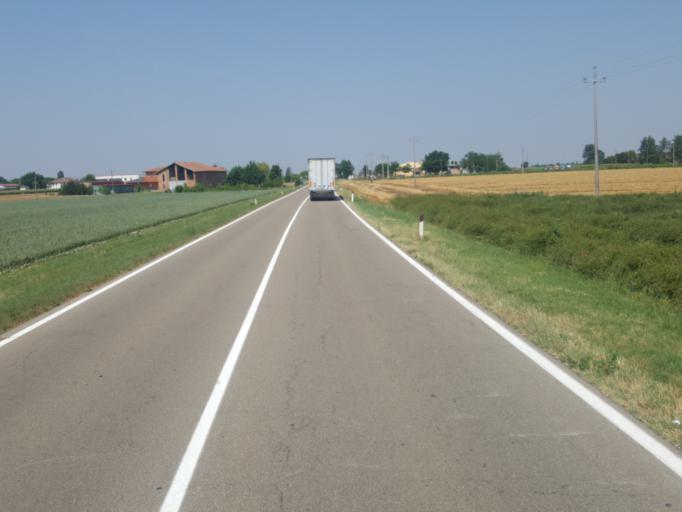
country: IT
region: Emilia-Romagna
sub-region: Provincia di Bologna
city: Sesto Imolese
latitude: 44.4671
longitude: 11.7181
